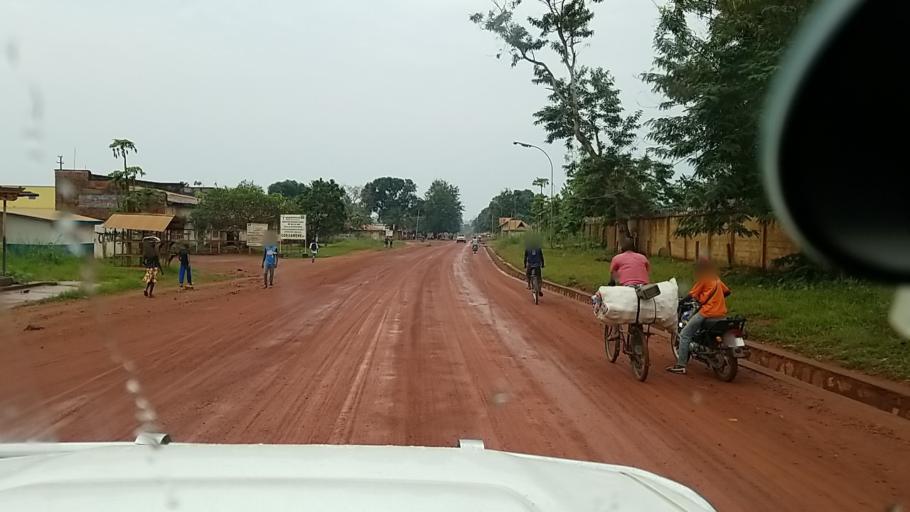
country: CD
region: Equateur
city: Gemena
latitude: 3.2403
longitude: 19.7809
